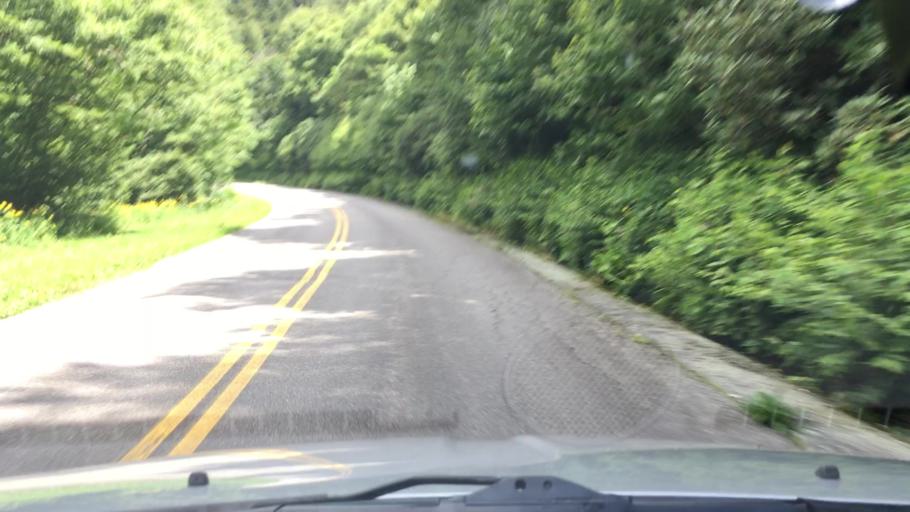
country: US
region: North Carolina
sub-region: Buncombe County
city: Black Mountain
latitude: 35.7073
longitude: -82.2726
